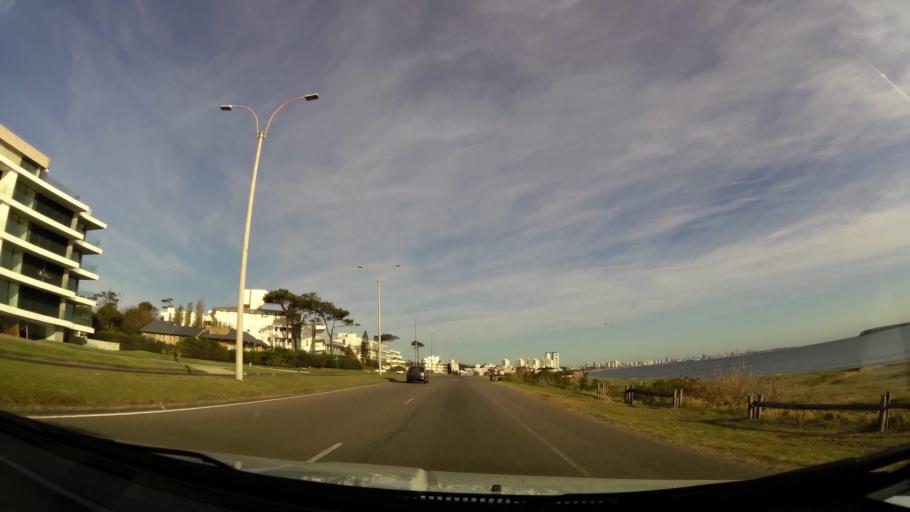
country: UY
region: Maldonado
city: Maldonado
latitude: -34.9167
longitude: -54.9769
